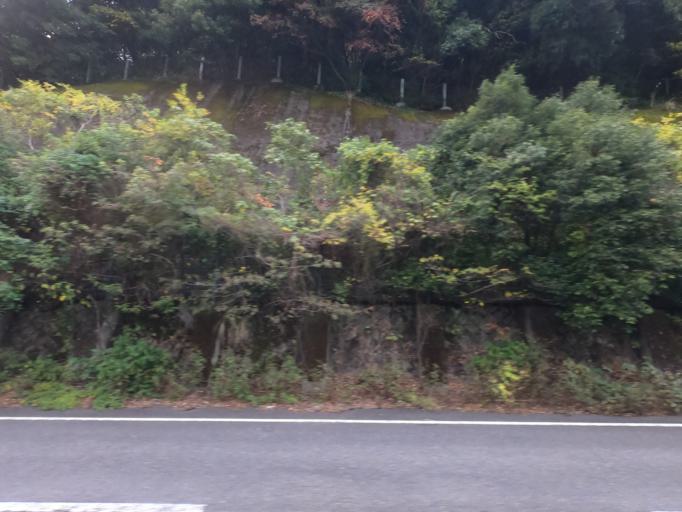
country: JP
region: Kumamoto
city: Minamata
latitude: 32.2425
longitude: 130.4843
